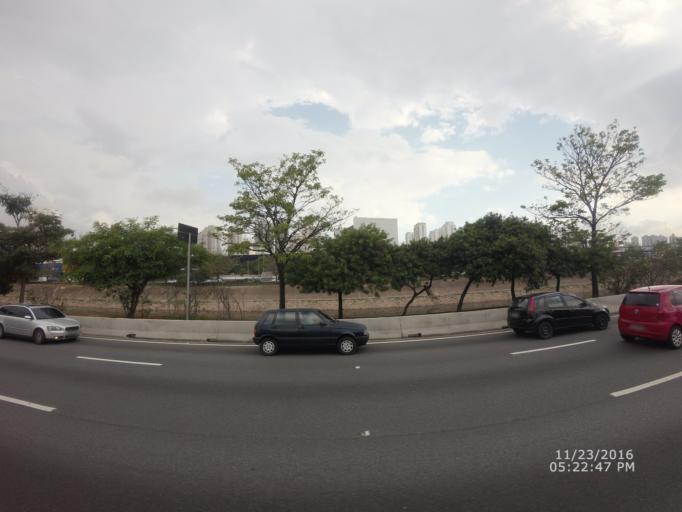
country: BR
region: Sao Paulo
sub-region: Sao Paulo
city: Sao Paulo
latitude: -23.5266
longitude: -46.5801
